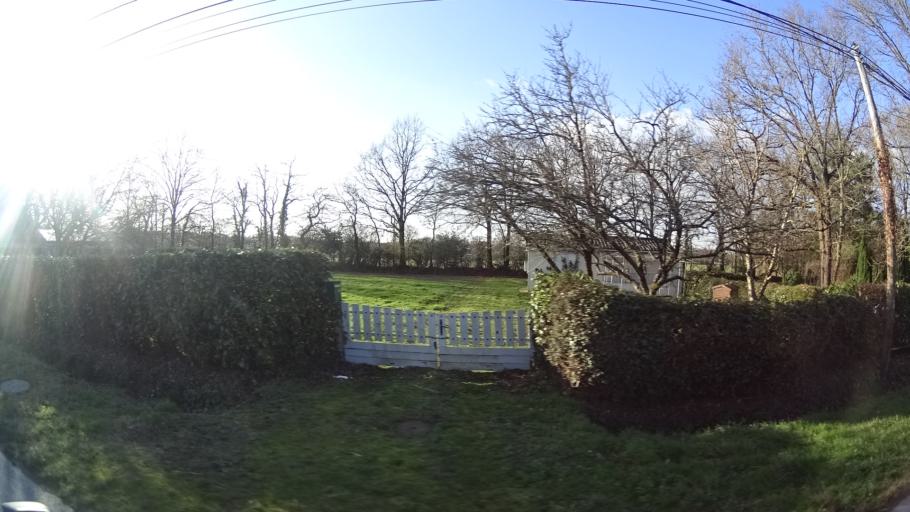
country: FR
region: Pays de la Loire
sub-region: Departement de la Loire-Atlantique
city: Plesse
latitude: 47.5310
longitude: -1.8863
